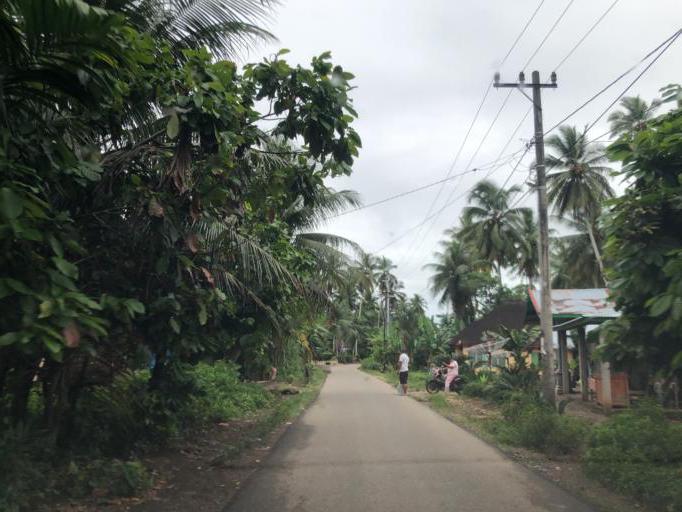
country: ID
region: West Sumatra
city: Pauhambar
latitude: -0.6251
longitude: 100.2136
